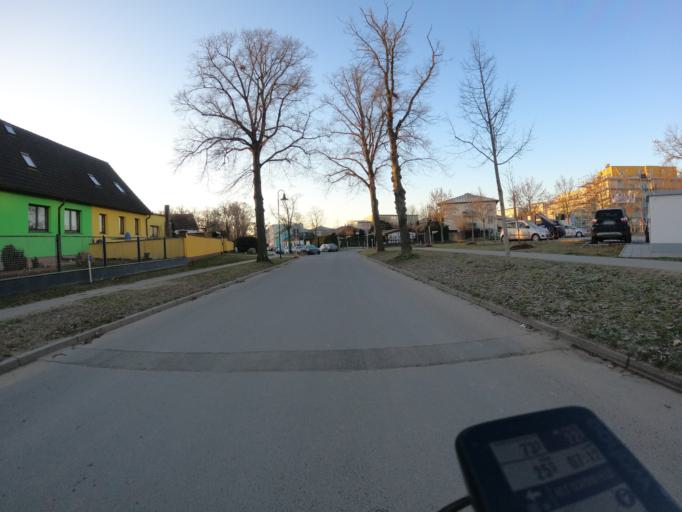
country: DE
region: Brandenburg
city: Schonefeld
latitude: 52.3904
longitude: 13.5027
